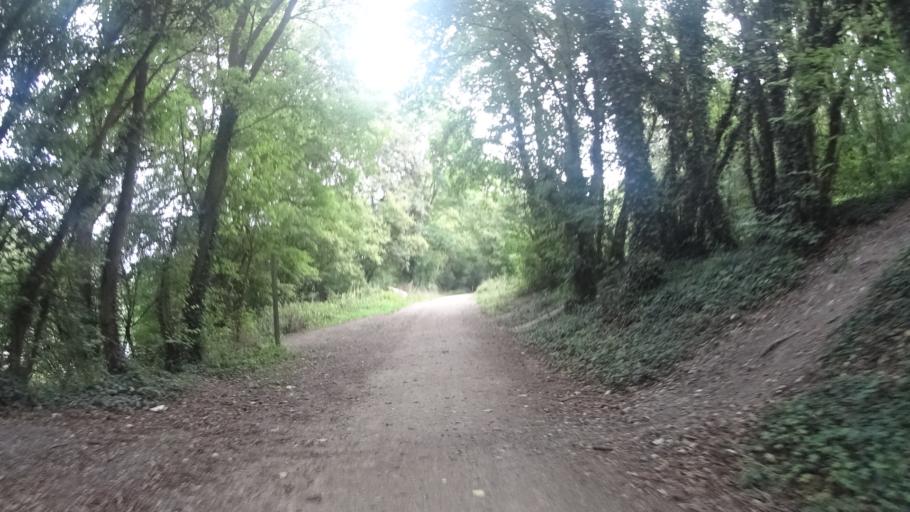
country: FR
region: Picardie
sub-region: Departement de l'Aisne
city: Origny-Sainte-Benoite
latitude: 49.8548
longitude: 3.4998
